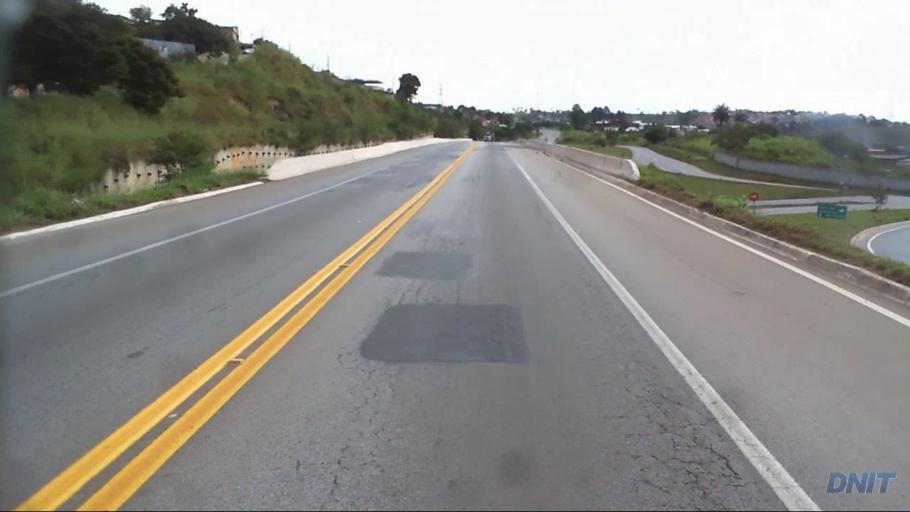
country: BR
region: Minas Gerais
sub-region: Santa Luzia
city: Santa Luzia
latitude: -19.8344
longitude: -43.8542
